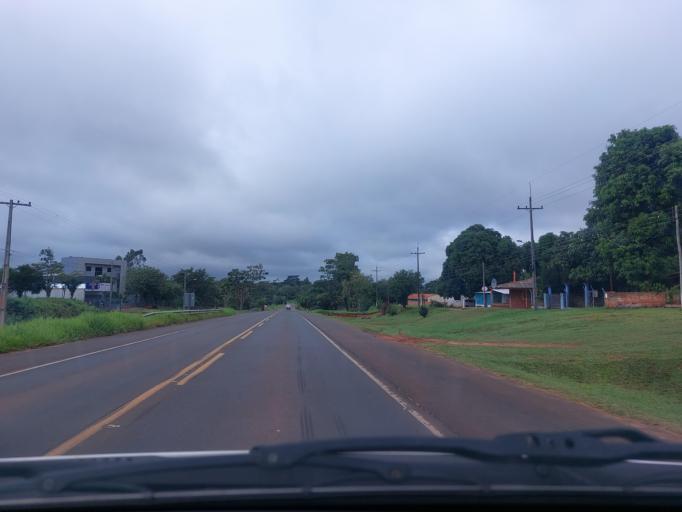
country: PY
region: San Pedro
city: Guayaybi
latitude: -24.6015
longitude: -56.3862
